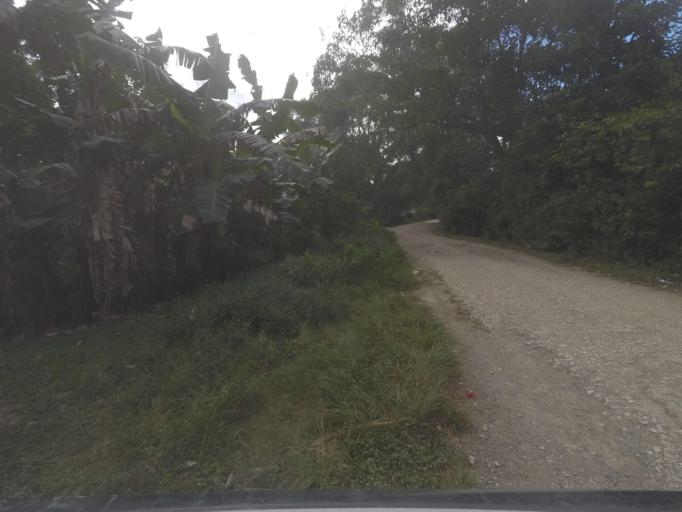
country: TL
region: Baucau
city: Venilale
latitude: -8.6386
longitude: 126.3818
